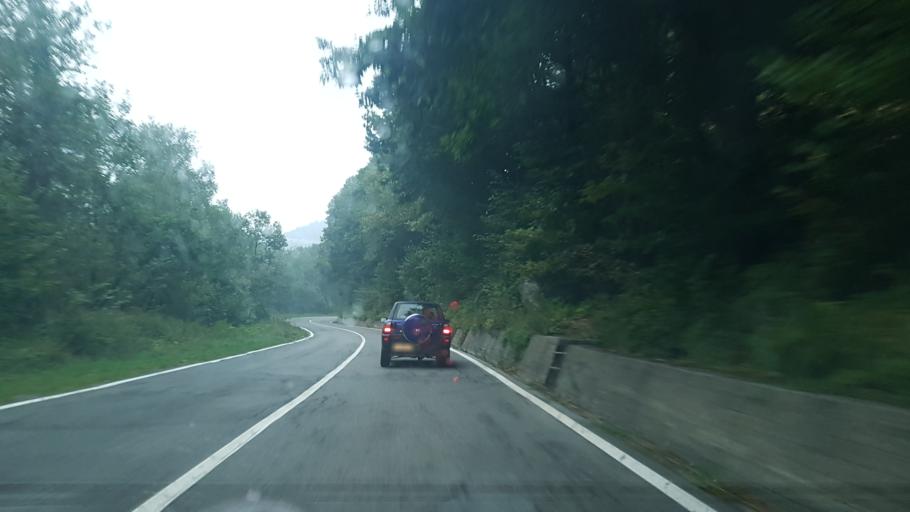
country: IT
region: Piedmont
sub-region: Provincia di Cuneo
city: Frabosa Soprana
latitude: 44.2704
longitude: 7.7693
